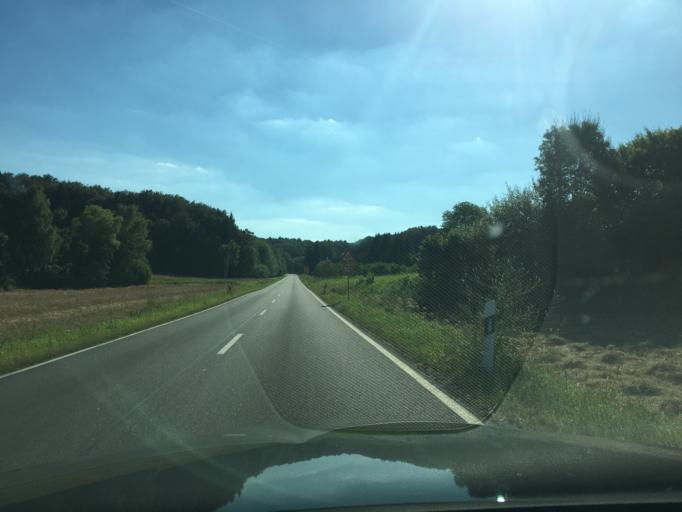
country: DE
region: Bavaria
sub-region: Upper Franconia
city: Obertrubach
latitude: 49.6722
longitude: 11.3541
